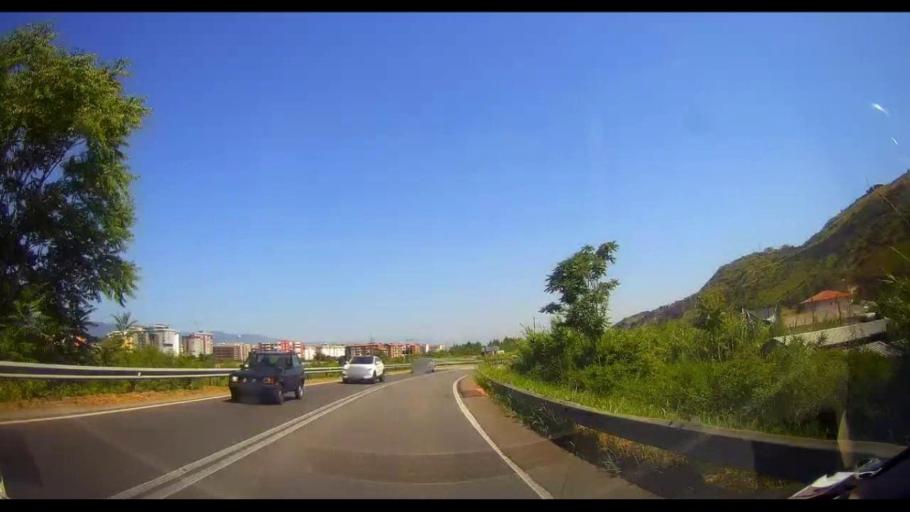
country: IT
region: Calabria
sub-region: Provincia di Cosenza
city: Cosenza
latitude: 39.3009
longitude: 16.2653
